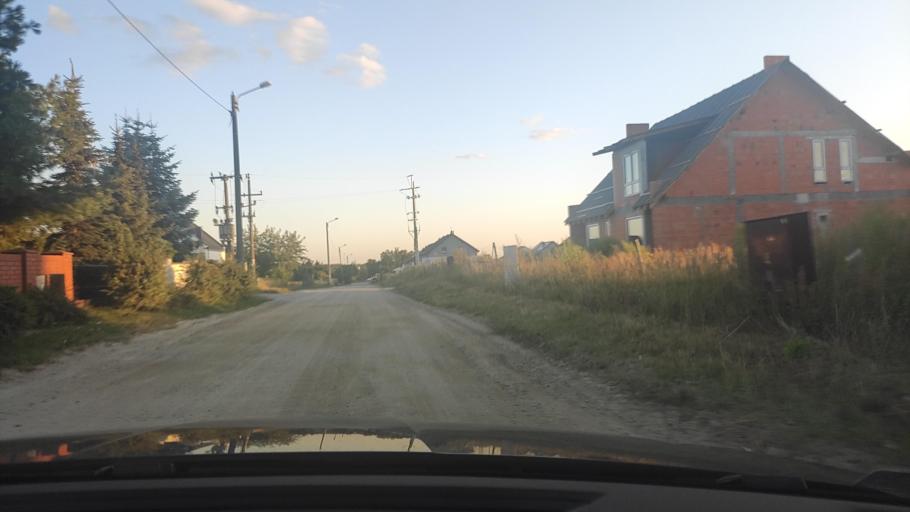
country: PL
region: Greater Poland Voivodeship
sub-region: Powiat poznanski
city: Swarzedz
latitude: 52.4298
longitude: 17.1131
